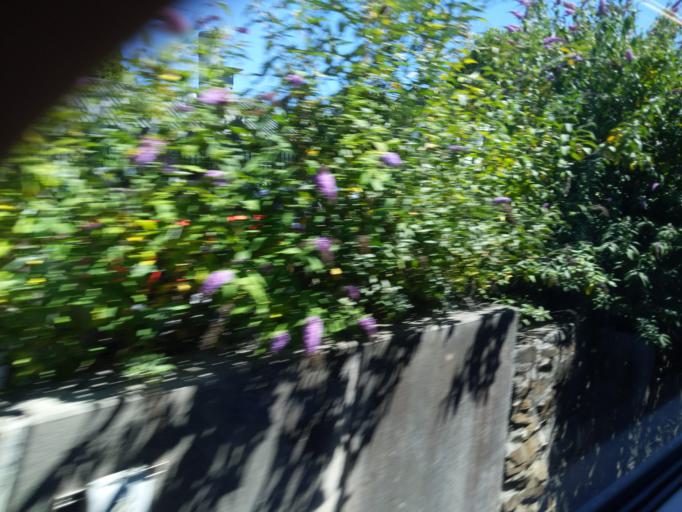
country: GB
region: England
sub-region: Cornwall
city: Redruth
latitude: 50.2366
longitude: -5.2247
